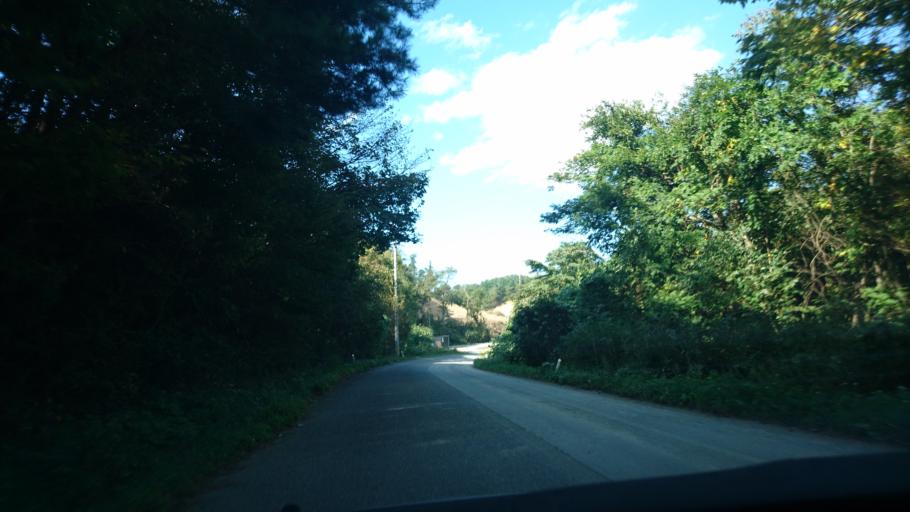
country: JP
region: Iwate
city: Ichinoseki
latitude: 38.8746
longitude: 141.0459
